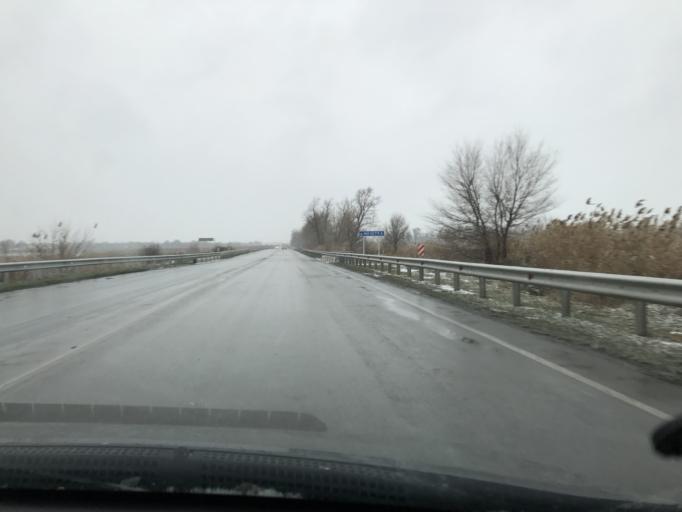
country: RU
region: Rostov
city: Mechetinskaya
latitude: 46.6666
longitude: 40.5419
